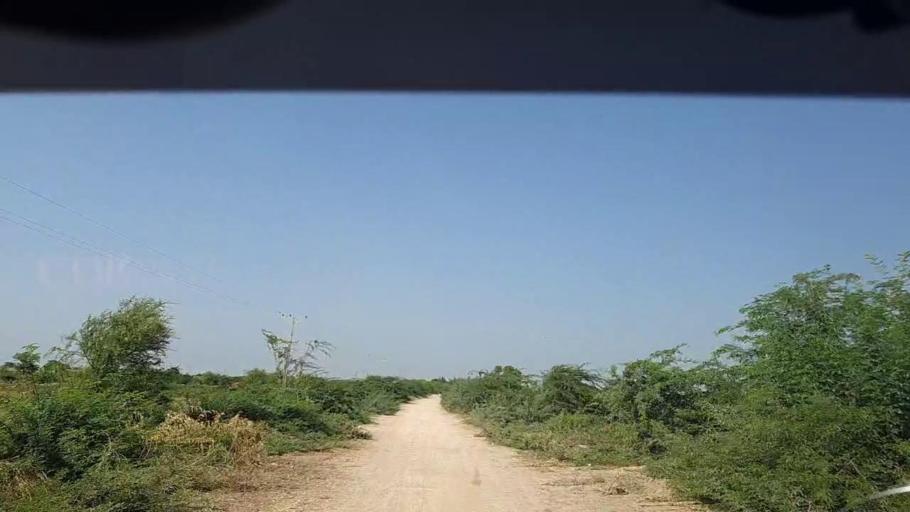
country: PK
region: Sindh
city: Badin
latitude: 24.4662
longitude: 68.7798
